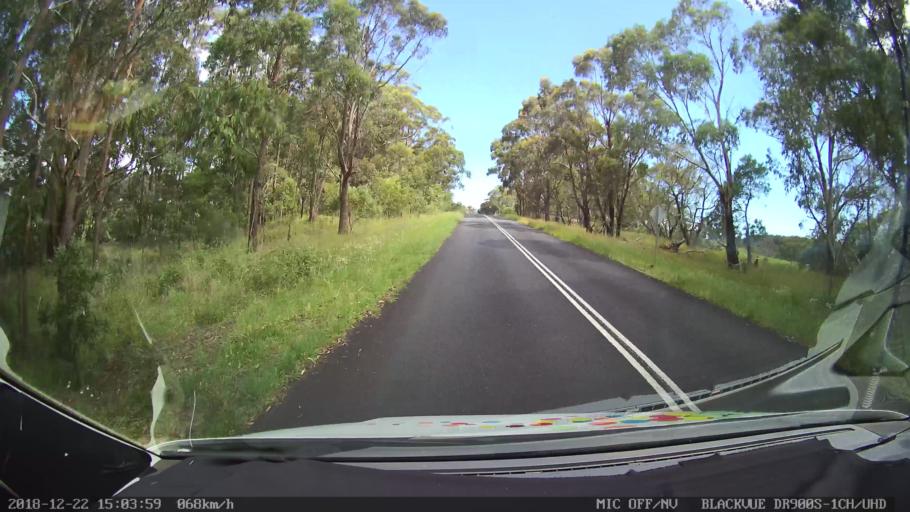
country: AU
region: New South Wales
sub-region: Bellingen
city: Dorrigo
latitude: -30.2701
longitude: 152.4385
